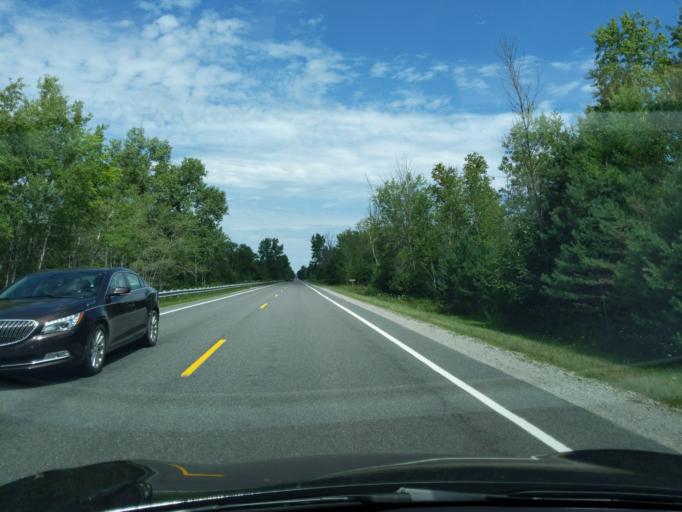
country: US
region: Michigan
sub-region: Midland County
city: Midland
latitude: 43.5447
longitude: -84.3697
